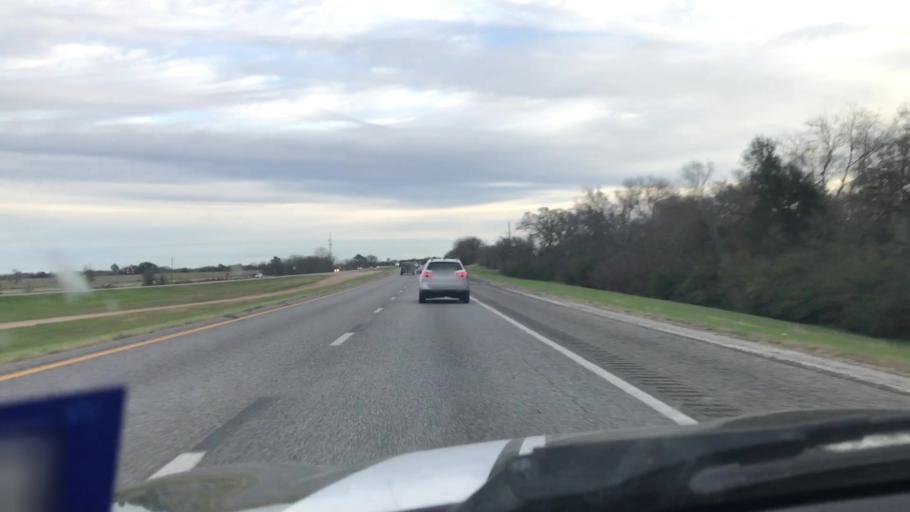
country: US
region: Texas
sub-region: Waller County
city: Hempstead
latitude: 30.1300
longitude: -96.1503
